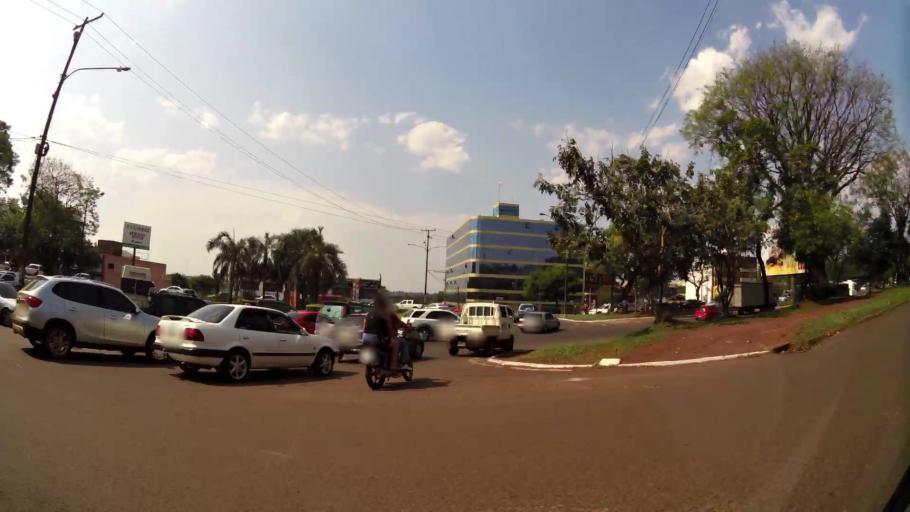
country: PY
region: Alto Parana
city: Ciudad del Este
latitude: -25.5109
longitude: -54.6295
